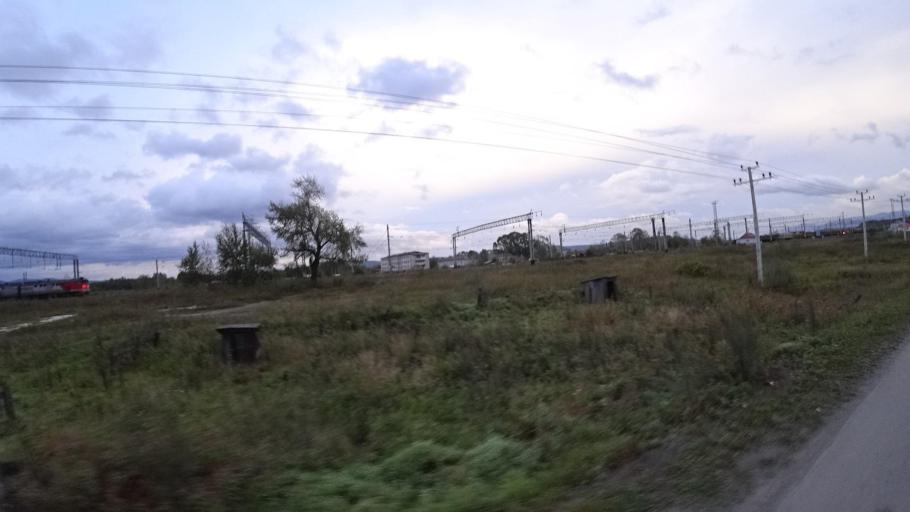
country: RU
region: Jewish Autonomous Oblast
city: Izvestkovyy
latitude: 48.9861
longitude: 131.5488
